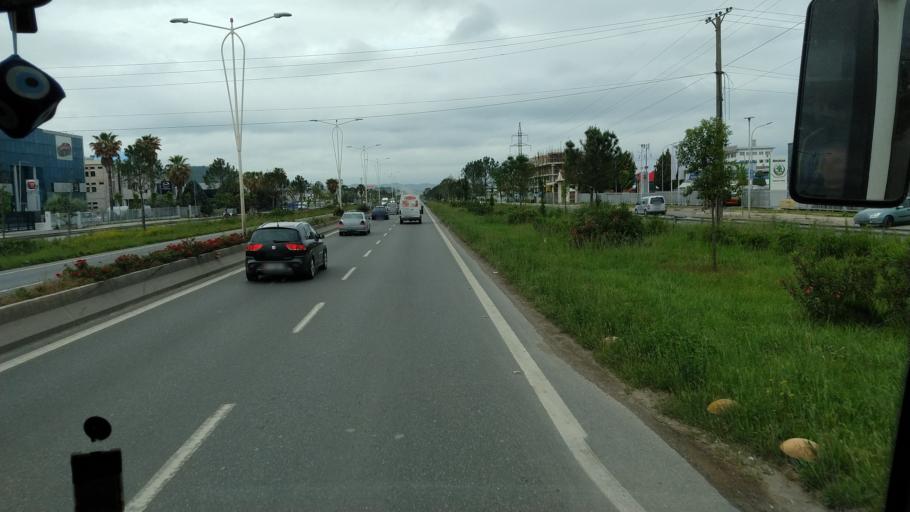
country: AL
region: Tirane
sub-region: Rrethi i Tiranes
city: Kamez
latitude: 41.3491
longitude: 19.7584
